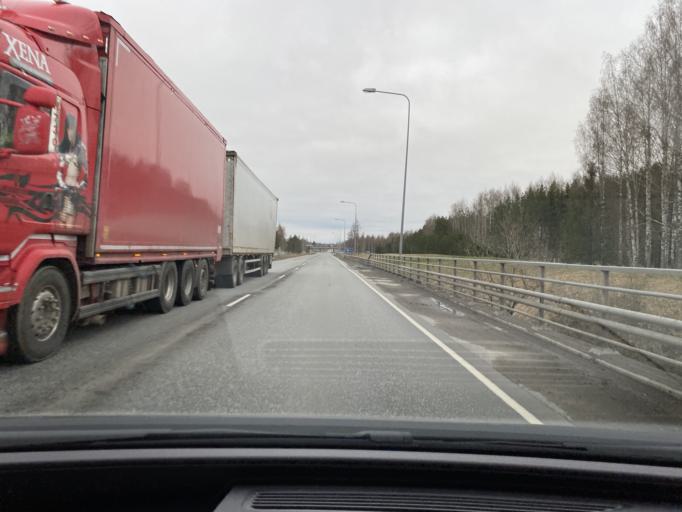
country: FI
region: Satakunta
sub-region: Pori
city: Huittinen
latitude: 61.1867
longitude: 22.6868
